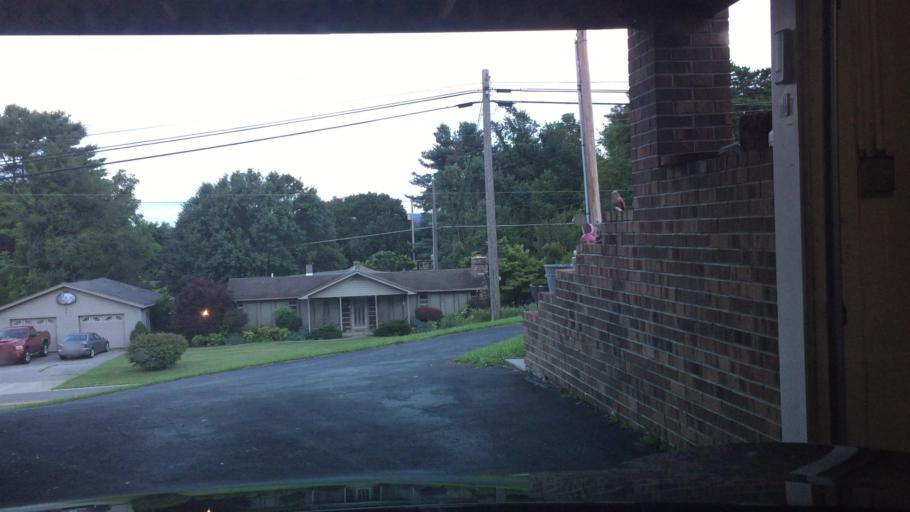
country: US
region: Virginia
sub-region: Pulaski County
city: Pulaski
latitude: 36.9526
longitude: -80.8792
